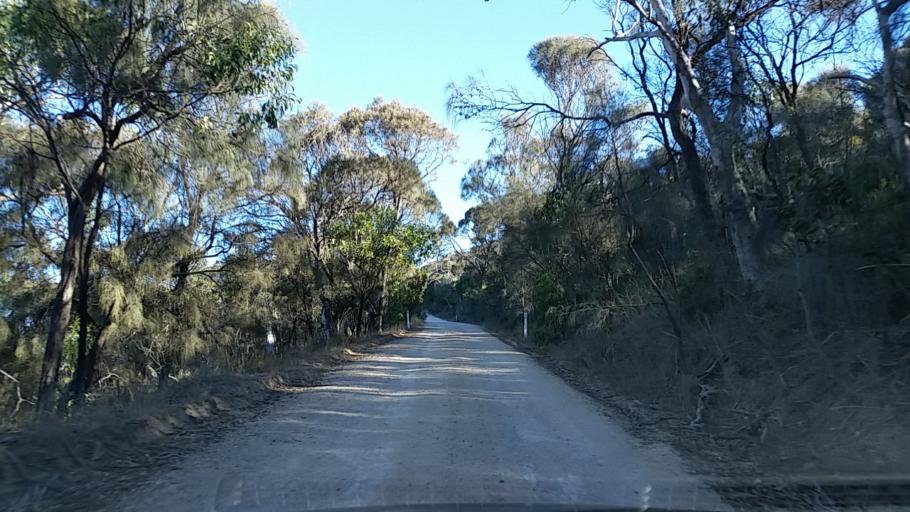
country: AU
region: South Australia
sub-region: Mount Barker
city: Nairne
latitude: -35.0632
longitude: 138.9239
